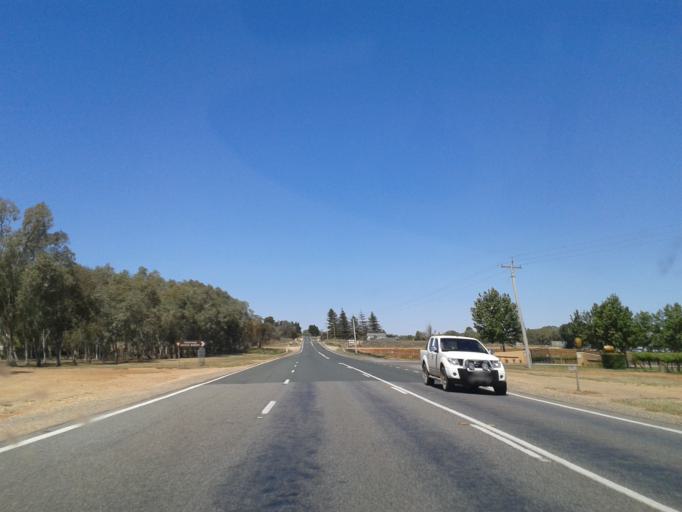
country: AU
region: New South Wales
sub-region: Wentworth
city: Gol Gol
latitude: -34.2289
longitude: 142.2485
